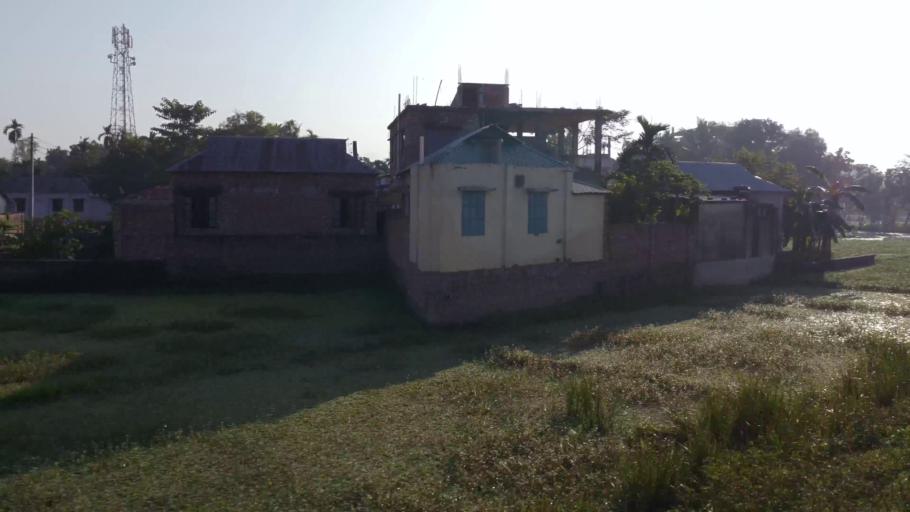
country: BD
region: Dhaka
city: Jamalpur
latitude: 24.8958
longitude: 89.9841
